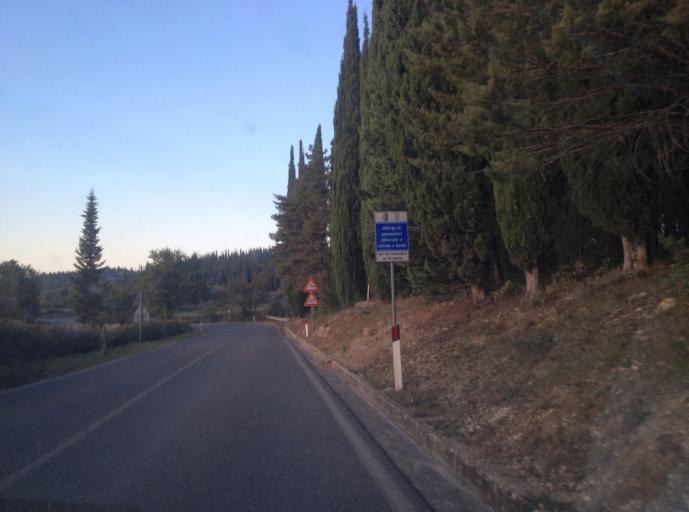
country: IT
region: Tuscany
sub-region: Provincia di Siena
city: Castellina in Chianti
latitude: 43.4398
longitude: 11.3012
